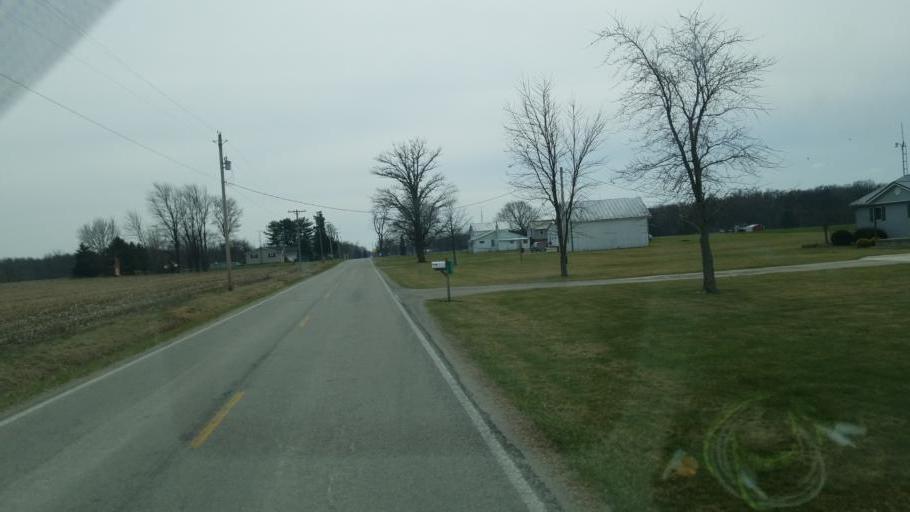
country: US
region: Ohio
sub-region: Huron County
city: Wakeman
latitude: 41.1796
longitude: -82.4903
